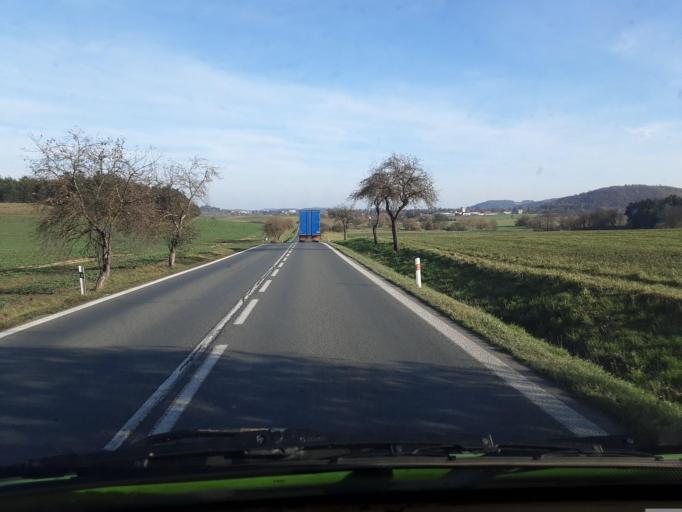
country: CZ
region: Plzensky
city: Horazd'ovice
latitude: 49.3301
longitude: 13.6591
